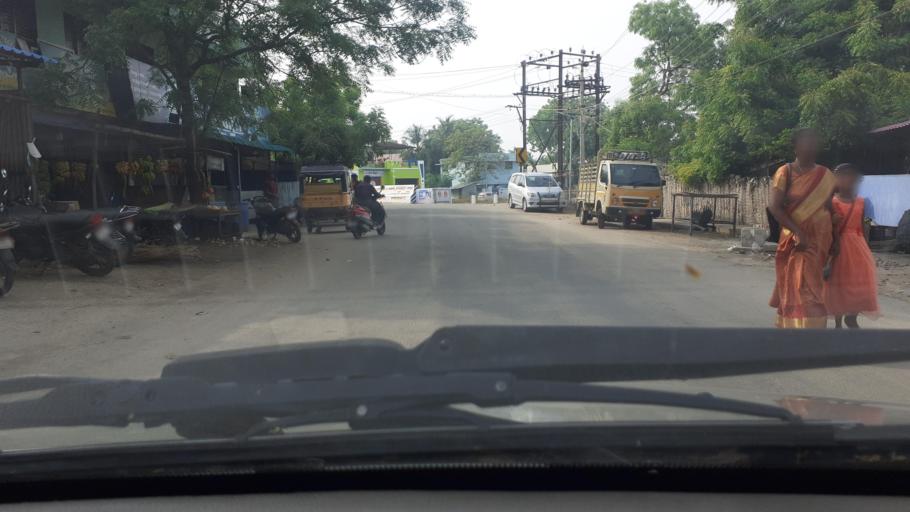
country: IN
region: Tamil Nadu
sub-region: Thoothukkudi
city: Korampallam
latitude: 8.7900
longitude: 78.1149
